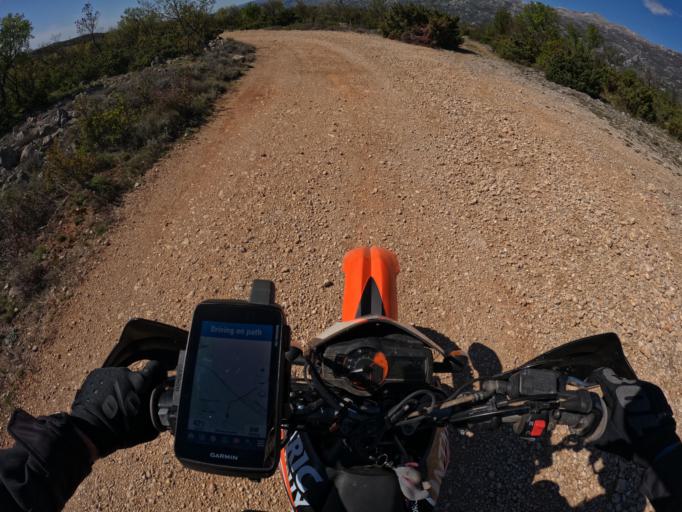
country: HR
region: Zadarska
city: Pridraga
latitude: 44.2372
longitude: 15.5591
